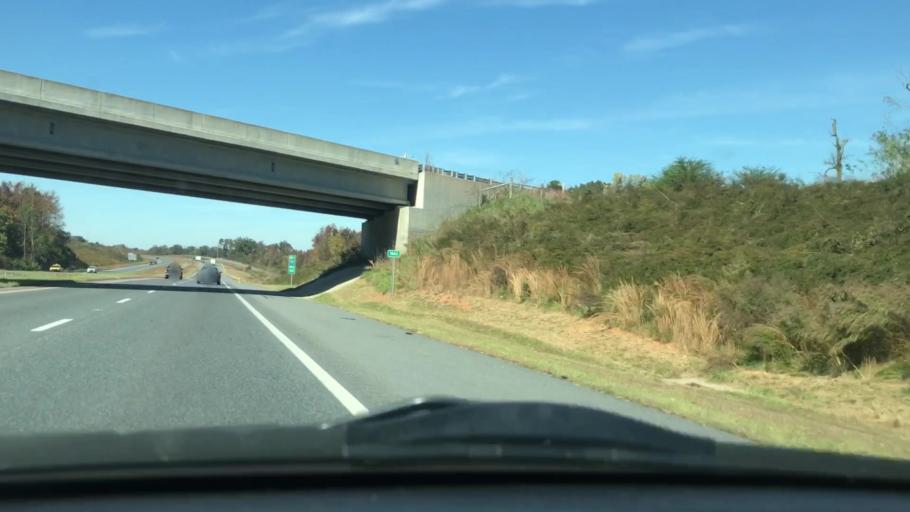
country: US
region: North Carolina
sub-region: Randolph County
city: Randleman
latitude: 35.8351
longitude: -79.8607
